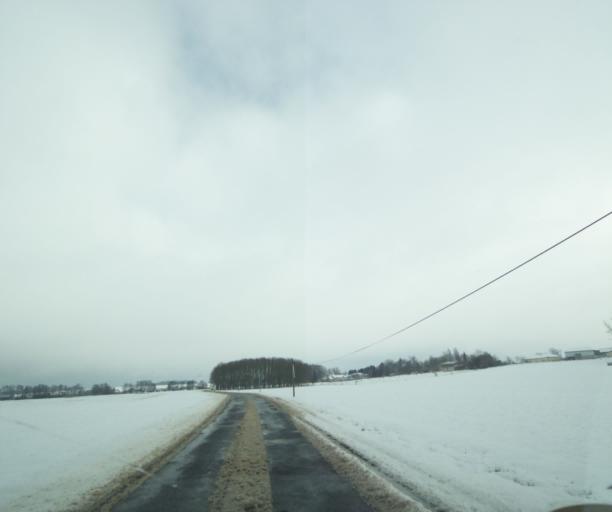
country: FR
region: Champagne-Ardenne
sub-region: Departement de la Haute-Marne
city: Montier-en-Der
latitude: 48.4964
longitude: 4.7179
